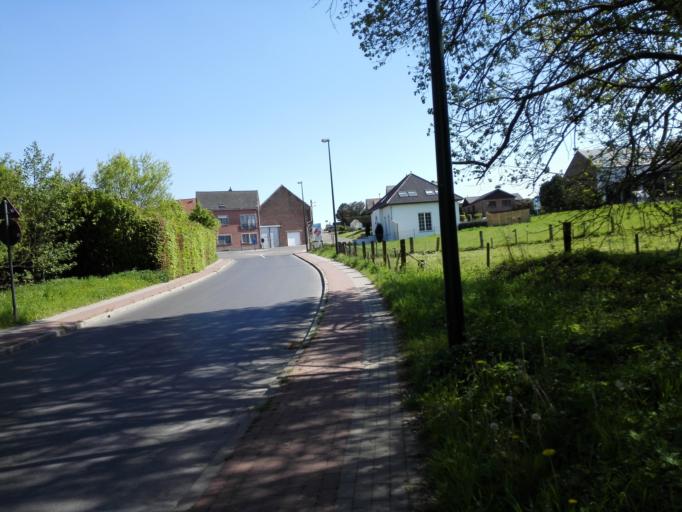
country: BE
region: Flanders
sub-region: Provincie Vlaams-Brabant
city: Tervuren
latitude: 50.8330
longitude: 4.5579
